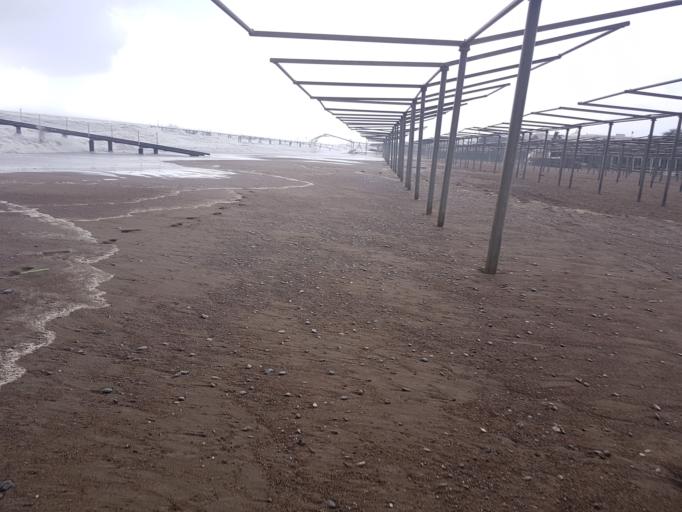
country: TR
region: Antalya
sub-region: Serik
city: Kumkoey
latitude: 36.8531
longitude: 30.8846
